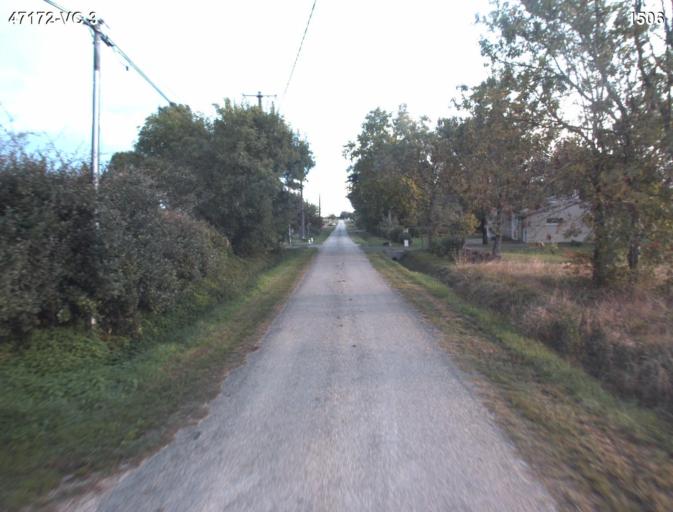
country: FR
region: Aquitaine
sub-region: Departement du Lot-et-Garonne
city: Sainte-Colombe-en-Bruilhois
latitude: 44.1572
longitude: 0.4945
